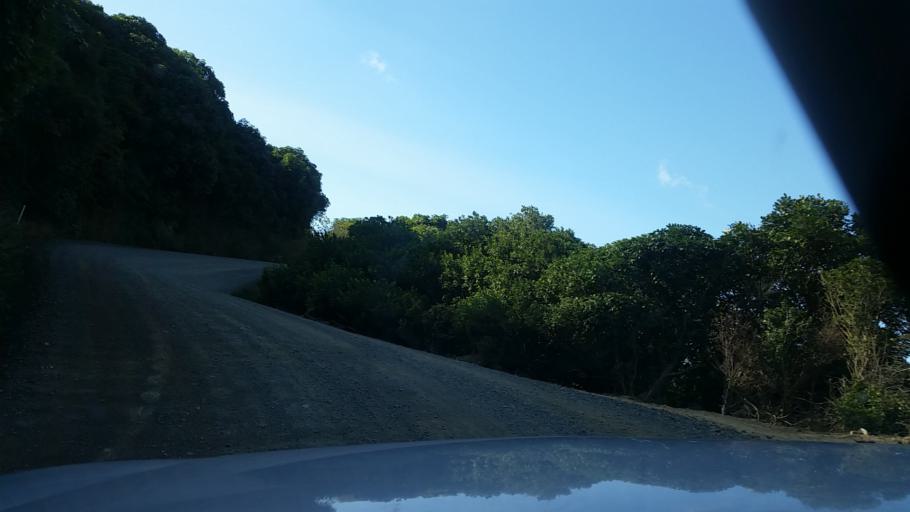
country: NZ
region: Marlborough
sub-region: Marlborough District
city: Picton
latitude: -41.2972
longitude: 174.1178
